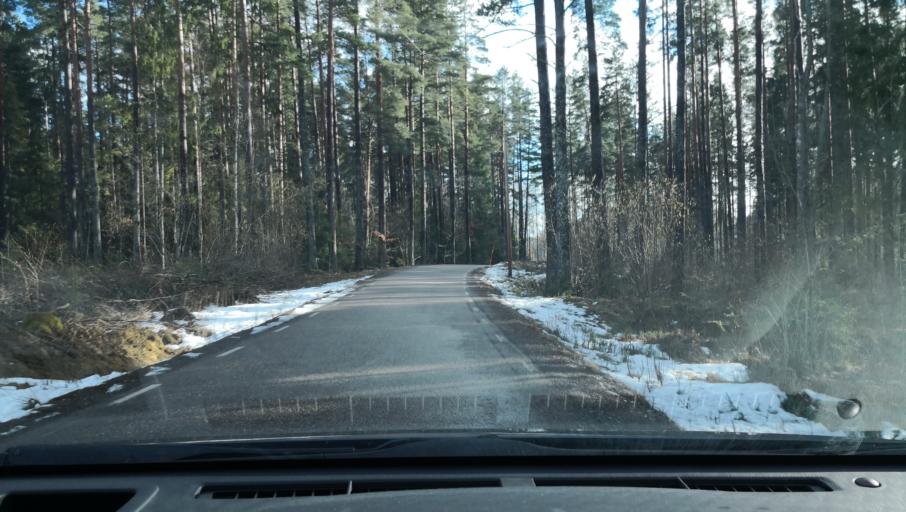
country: SE
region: Vaestmanland
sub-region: Arboga Kommun
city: Arboga
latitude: 59.3261
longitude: 15.7563
